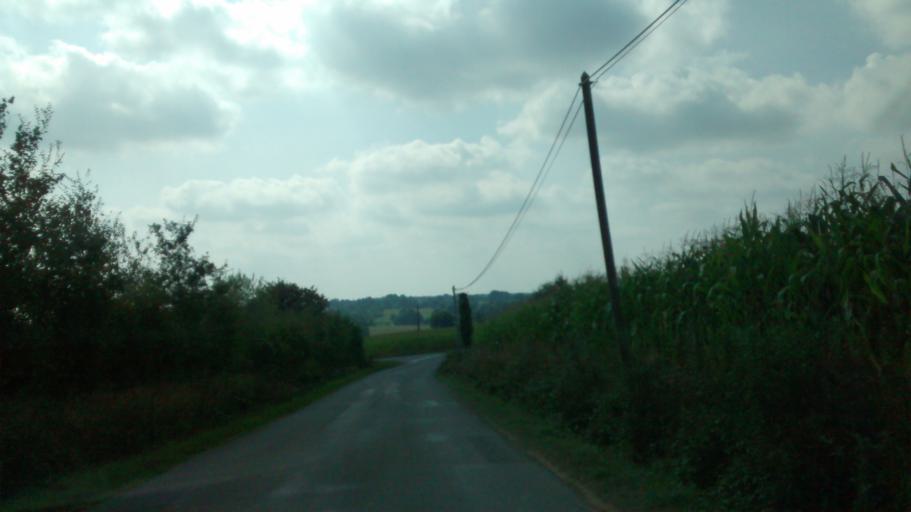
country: FR
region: Brittany
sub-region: Departement d'Ille-et-Vilaine
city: Livre-sur-Changeon
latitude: 48.2213
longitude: -1.3254
